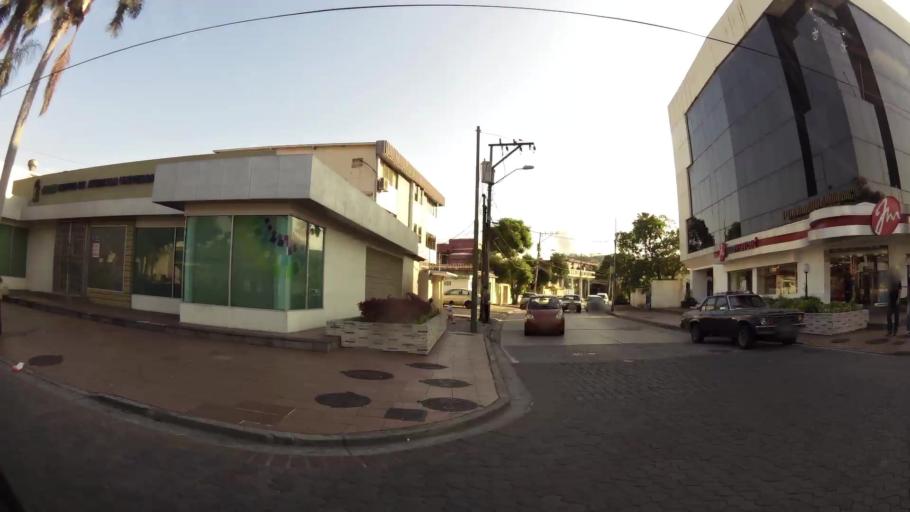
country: EC
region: Guayas
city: Guayaquil
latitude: -2.1744
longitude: -79.9059
